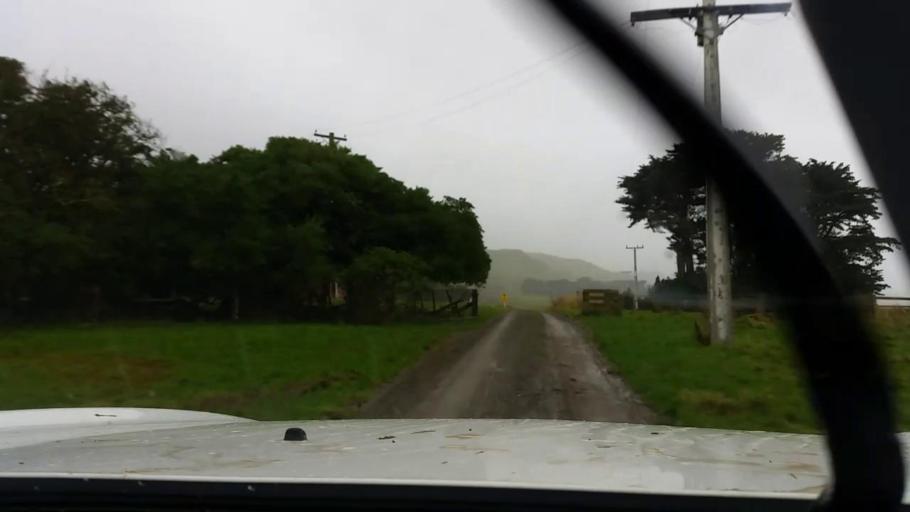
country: NZ
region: Wellington
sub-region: Masterton District
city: Masterton
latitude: -41.2623
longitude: 175.8948
